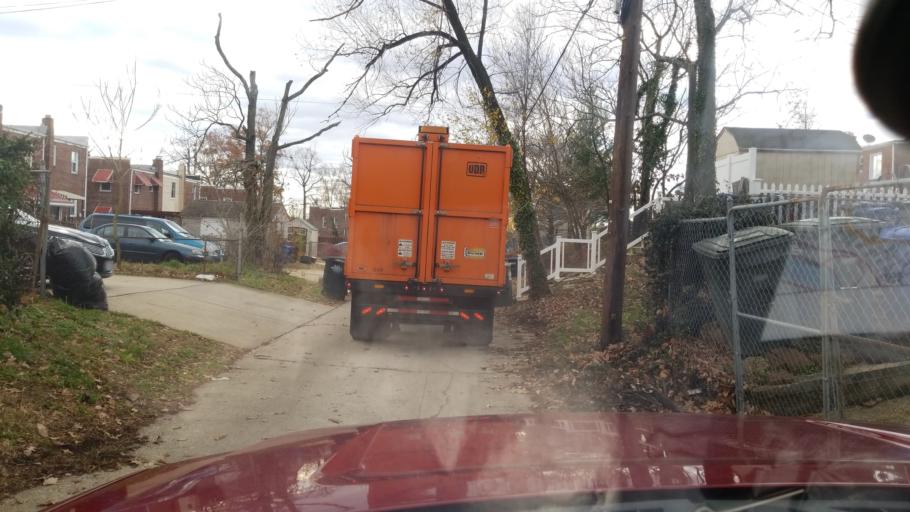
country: US
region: Maryland
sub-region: Prince George's County
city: Coral Hills
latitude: 38.8678
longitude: -76.9432
